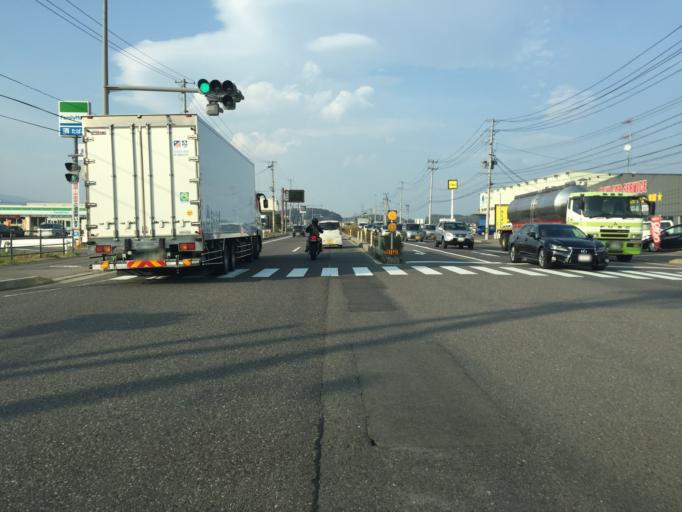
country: JP
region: Fukushima
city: Motomiya
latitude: 37.5323
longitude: 140.3965
